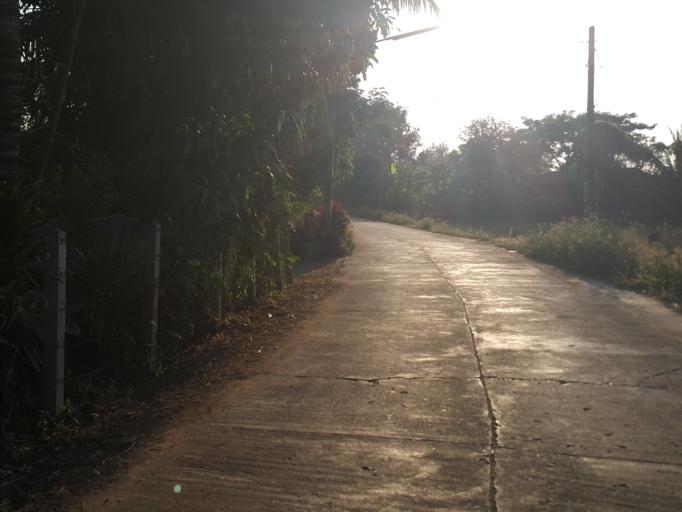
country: TH
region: Chiang Mai
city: Mae On
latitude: 18.7558
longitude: 99.2556
